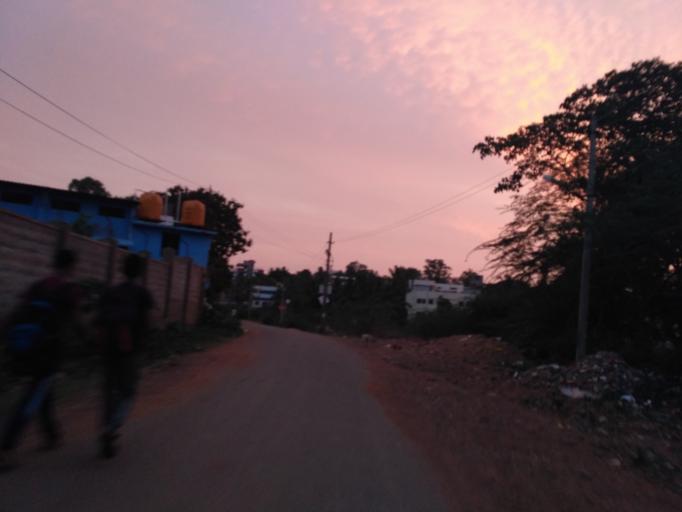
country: IN
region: Karnataka
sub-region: Dharwad
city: Hubli
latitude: 15.4423
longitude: 75.0181
